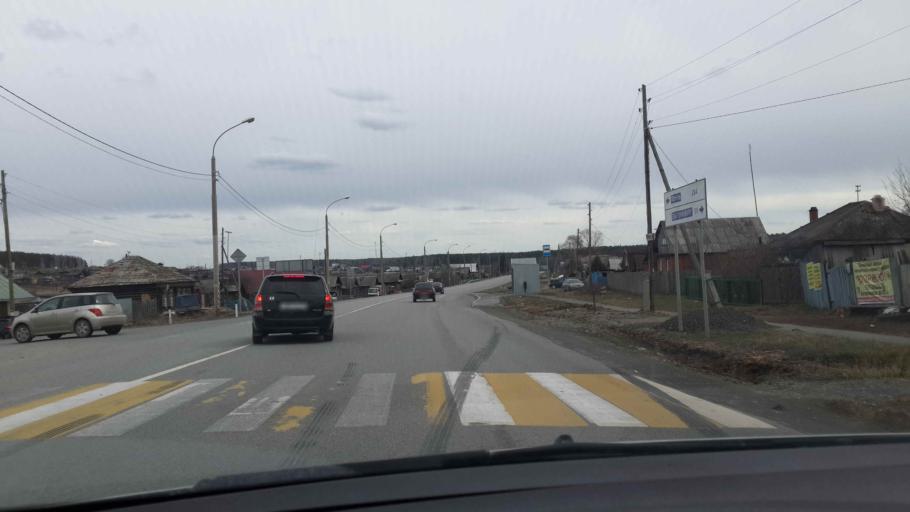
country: RU
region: Sverdlovsk
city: Beloyarskiy
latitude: 56.7713
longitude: 61.4476
